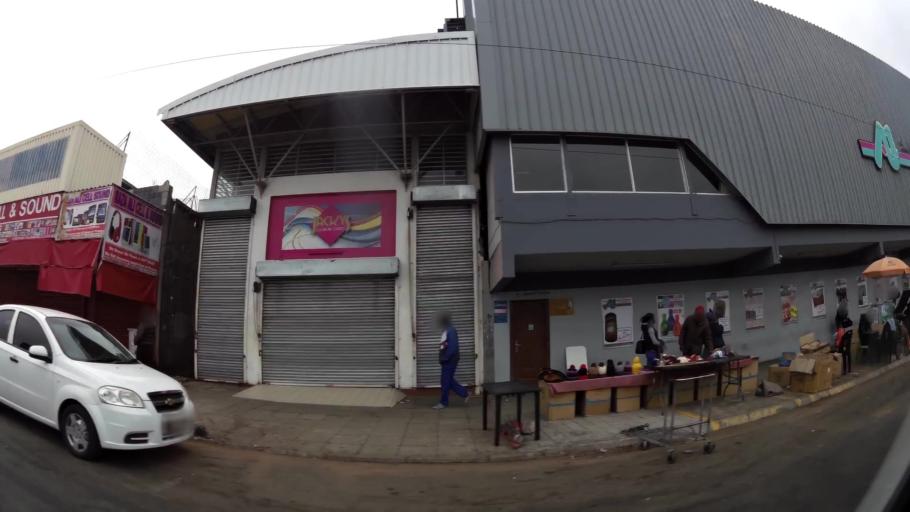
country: ZA
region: Limpopo
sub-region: Capricorn District Municipality
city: Polokwane
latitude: -23.9051
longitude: 29.4501
